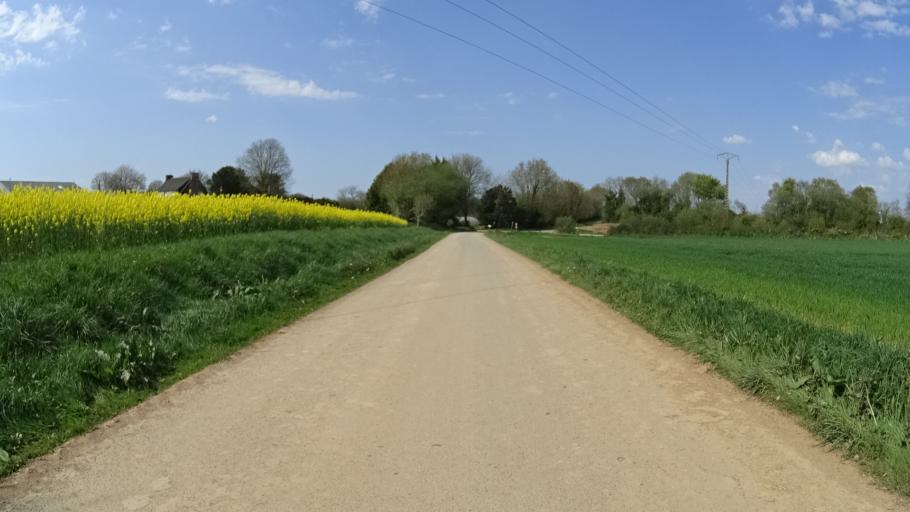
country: FR
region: Brittany
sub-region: Departement du Finistere
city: Sizun
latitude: 48.4262
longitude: -4.0910
